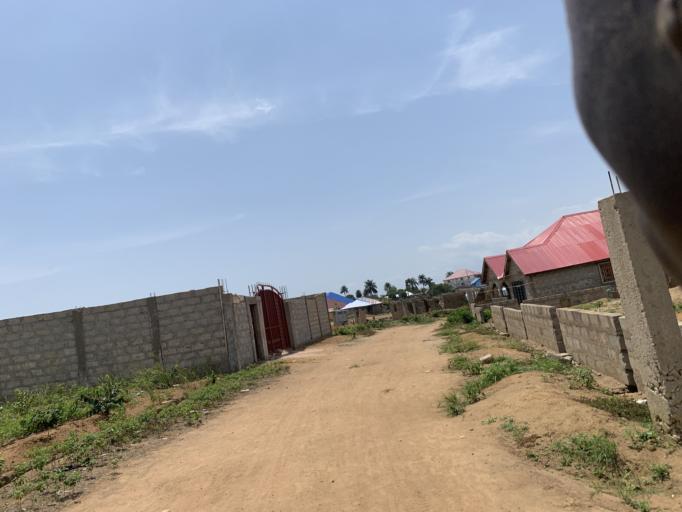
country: SL
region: Western Area
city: Waterloo
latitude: 8.3406
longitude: -13.0362
